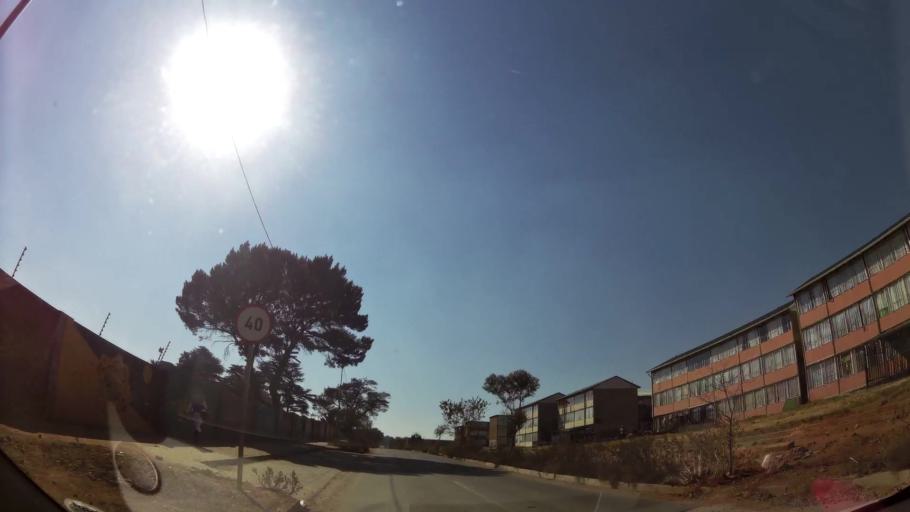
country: ZA
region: Gauteng
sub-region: City of Johannesburg Metropolitan Municipality
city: Johannesburg
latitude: -26.1833
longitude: 27.9689
